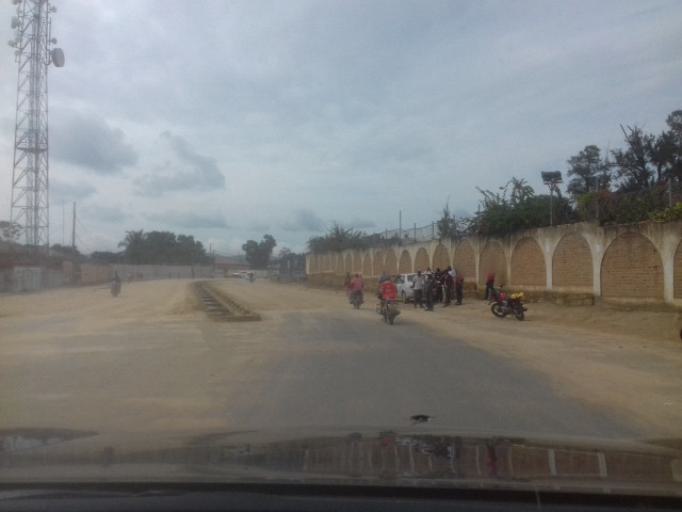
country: CD
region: Eastern Province
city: Bunia
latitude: 1.5524
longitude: 30.2477
